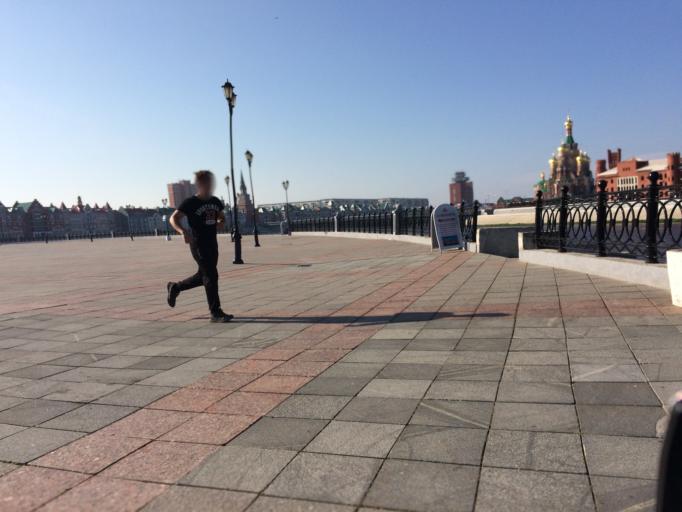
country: RU
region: Mariy-El
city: Yoshkar-Ola
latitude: 56.6372
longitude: 47.9059
